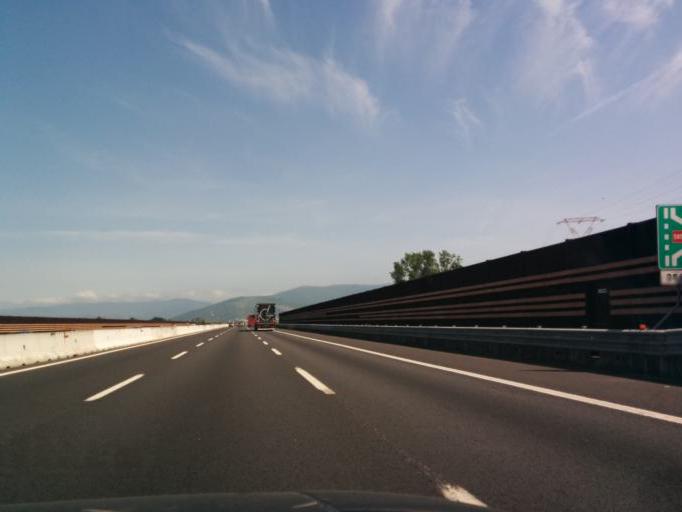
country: IT
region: Tuscany
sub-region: Province of Florence
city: San Donnino
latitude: 43.7969
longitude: 11.1562
